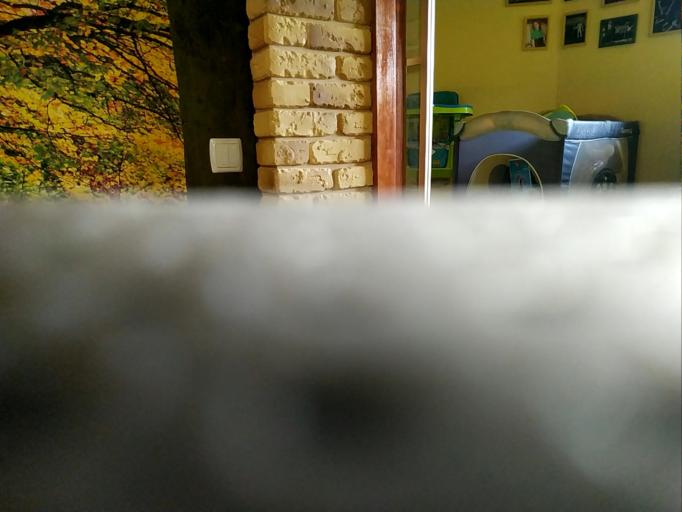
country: RU
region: Kaluga
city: Sukhinichi
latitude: 54.0810
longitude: 35.2867
